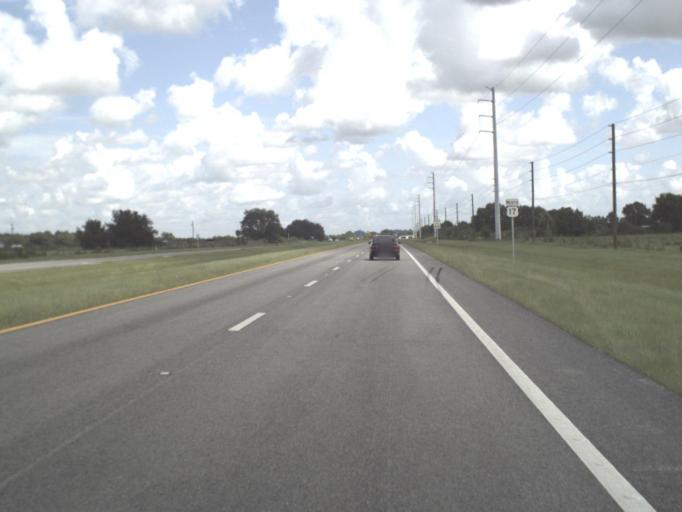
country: US
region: Florida
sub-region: Charlotte County
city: Harbour Heights
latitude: 27.0681
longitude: -81.9580
